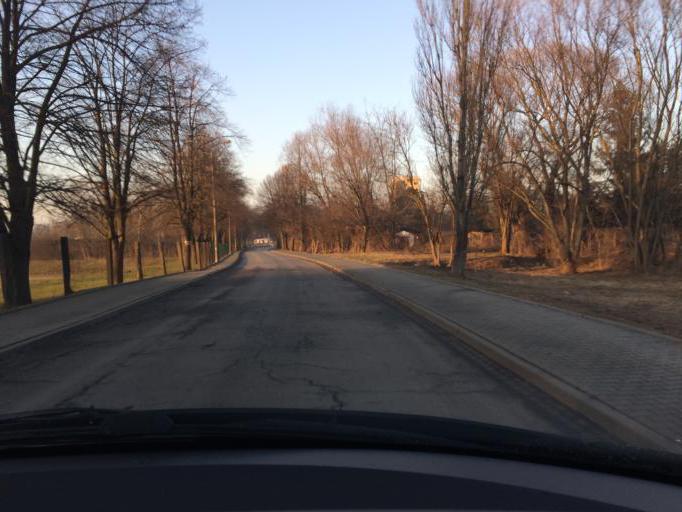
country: PL
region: Lesser Poland Voivodeship
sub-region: Powiat wielicki
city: Czarnochowice
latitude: 50.0102
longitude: 20.0413
